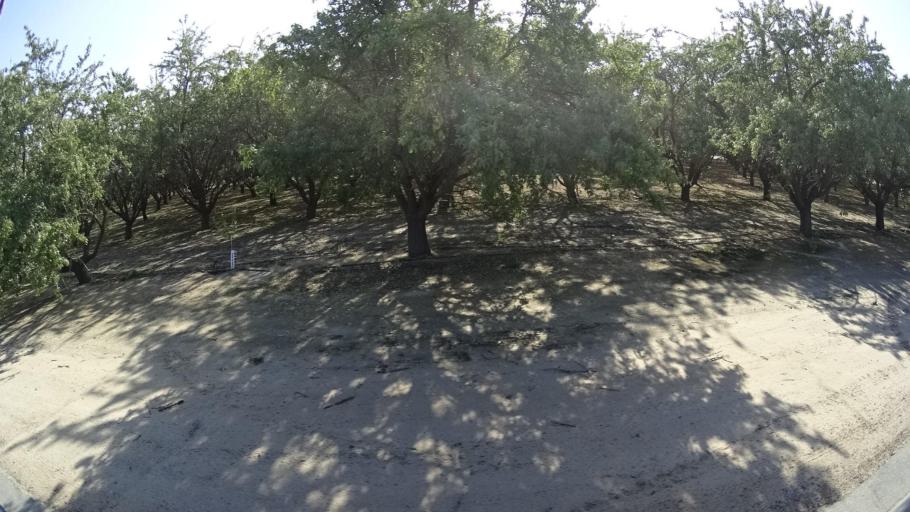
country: US
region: California
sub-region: Kern County
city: Shafter
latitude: 35.5297
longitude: -119.1508
